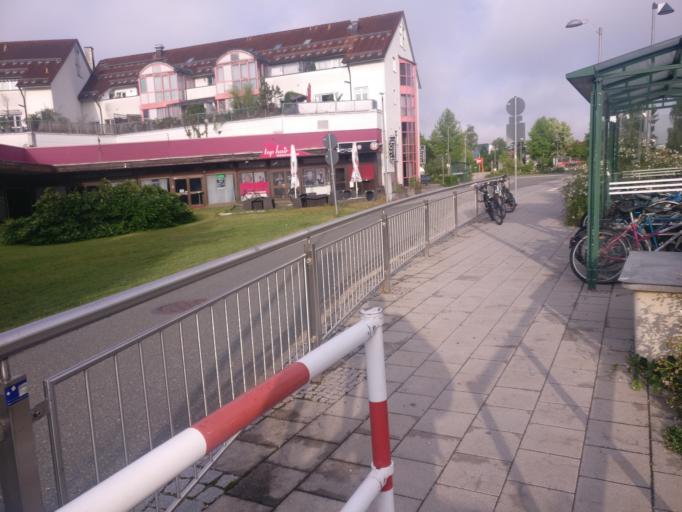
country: DE
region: Bavaria
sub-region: Upper Bavaria
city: Traunreut
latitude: 47.9650
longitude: 12.5905
